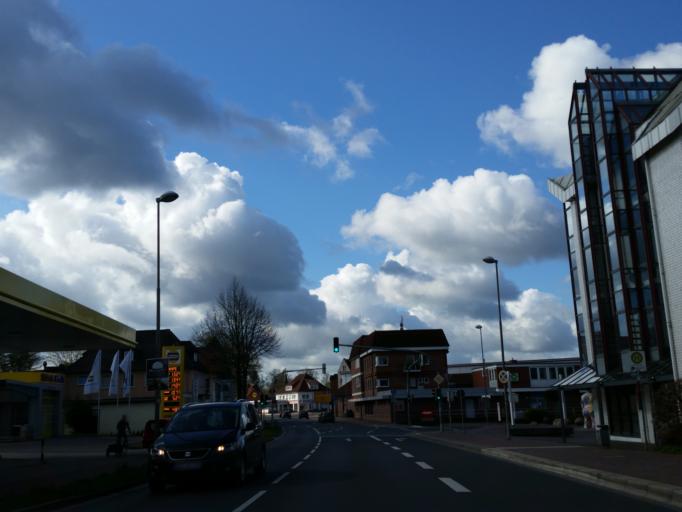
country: DE
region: Lower Saxony
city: Rotenburg
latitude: 53.1055
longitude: 9.3974
